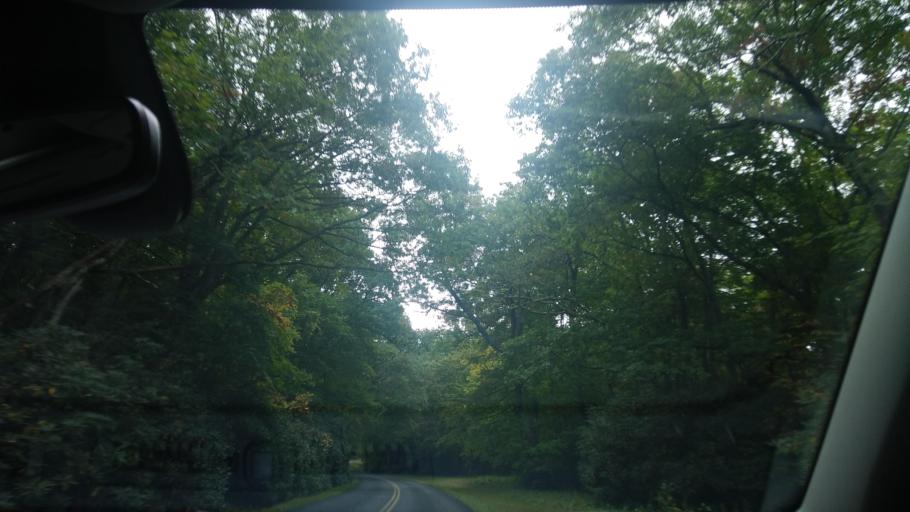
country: US
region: Virginia
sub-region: Carroll County
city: Cana
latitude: 36.6505
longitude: -80.5520
